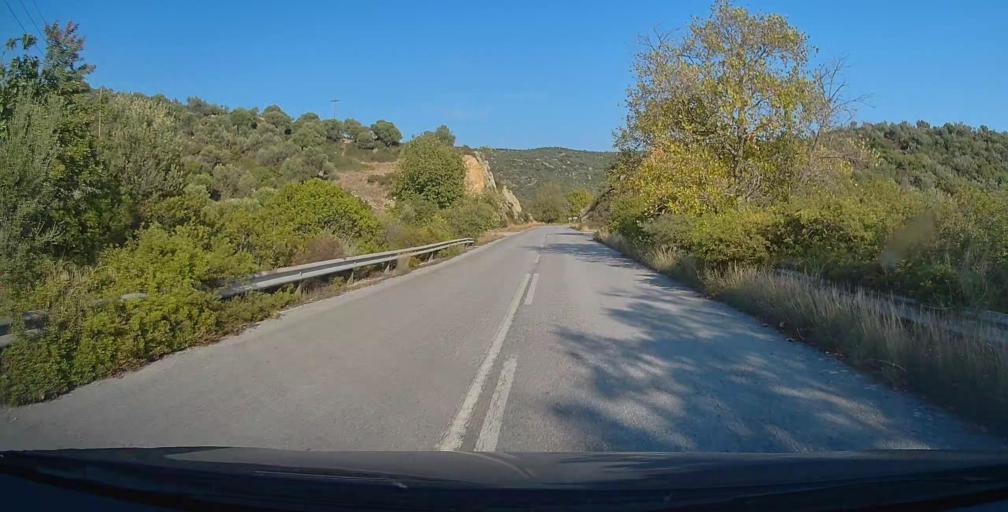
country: GR
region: Central Macedonia
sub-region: Nomos Chalkidikis
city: Sykia
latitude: 40.0059
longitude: 23.8816
